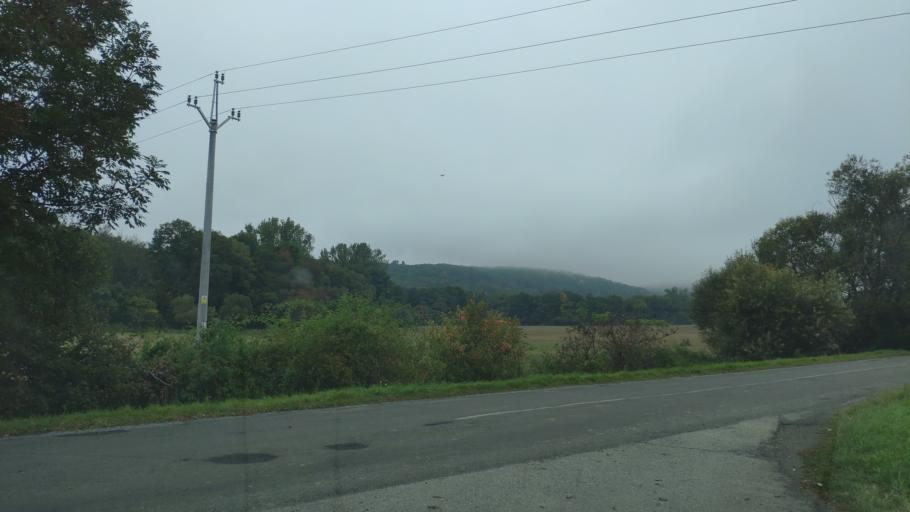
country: SK
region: Kosicky
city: Kosice
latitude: 48.8425
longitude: 21.4208
